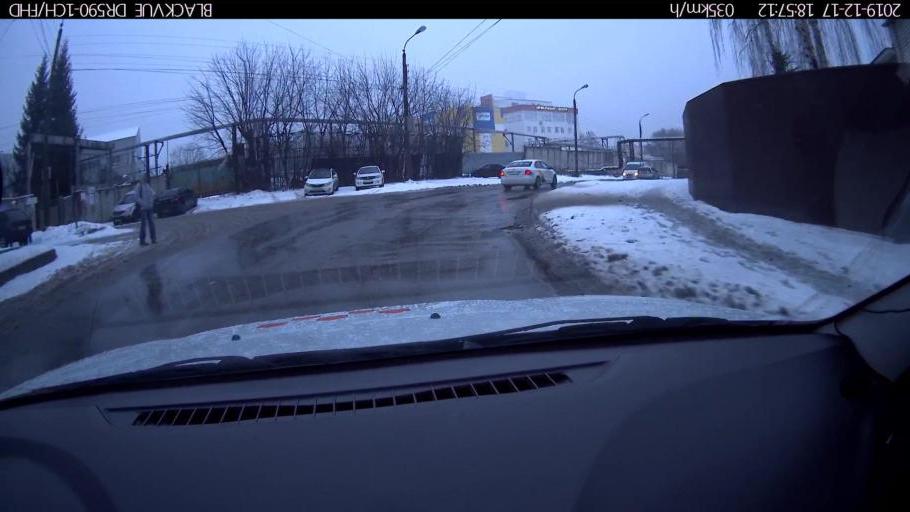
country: RU
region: Nizjnij Novgorod
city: Nizhniy Novgorod
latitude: 56.2883
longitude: 44.0002
